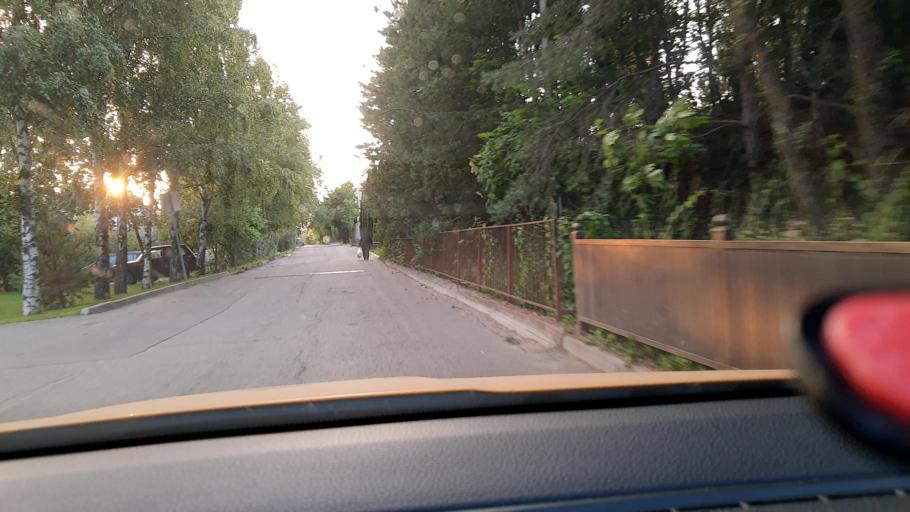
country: RU
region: Moskovskaya
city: Barvikha
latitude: 55.7247
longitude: 37.2975
